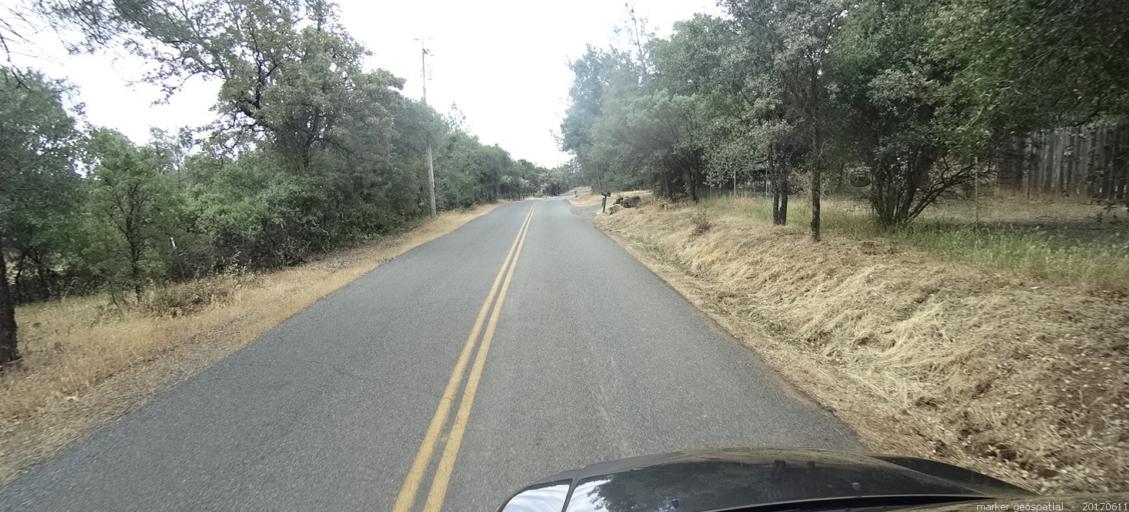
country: US
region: California
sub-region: Butte County
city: Berry Creek
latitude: 39.6387
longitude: -121.5284
